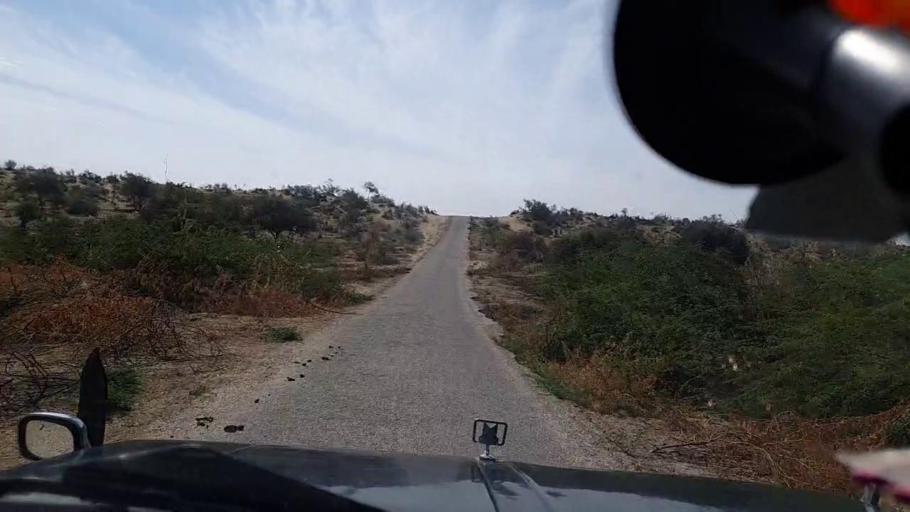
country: PK
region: Sindh
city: Diplo
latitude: 24.4038
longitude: 69.5879
